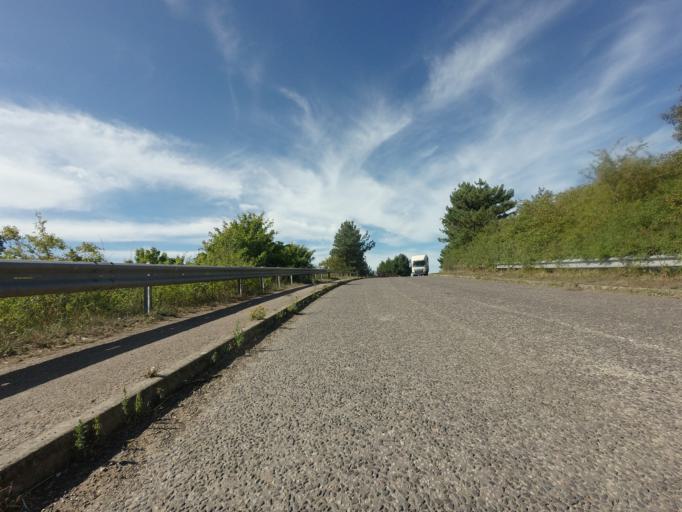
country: GB
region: England
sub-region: Kent
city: Birchington-on-Sea
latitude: 51.3585
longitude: 1.2447
